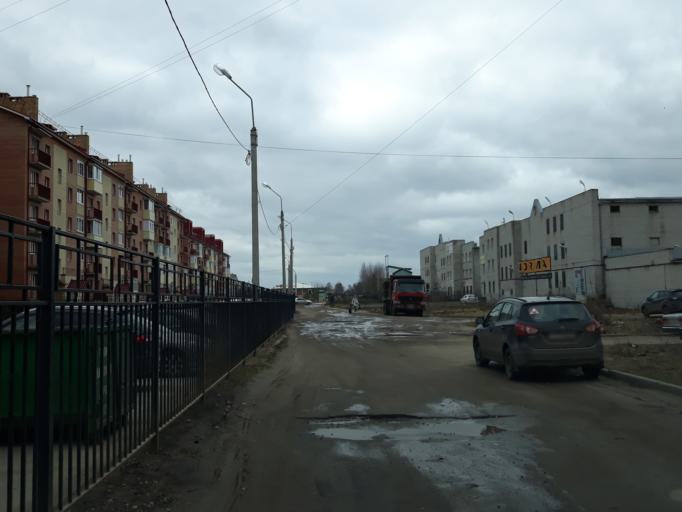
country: RU
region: Jaroslavl
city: Yaroslavl
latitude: 57.6507
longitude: 39.9674
